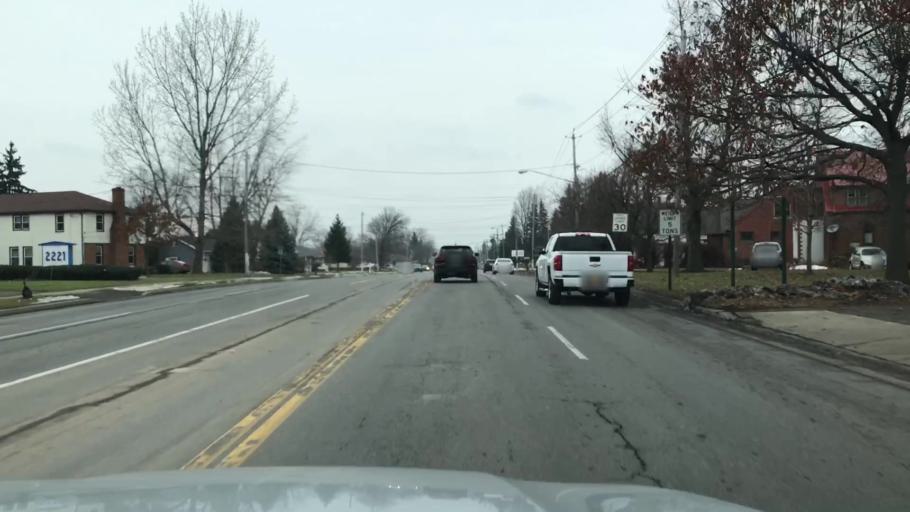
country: US
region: New York
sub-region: Erie County
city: Blasdell
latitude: 42.8047
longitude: -78.7974
